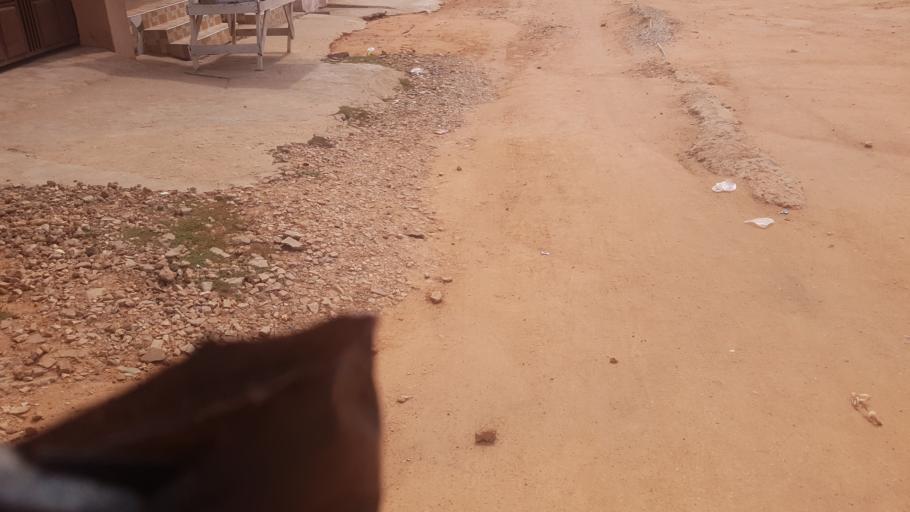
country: GH
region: Greater Accra
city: Gbawe
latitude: 5.5499
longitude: -0.3478
